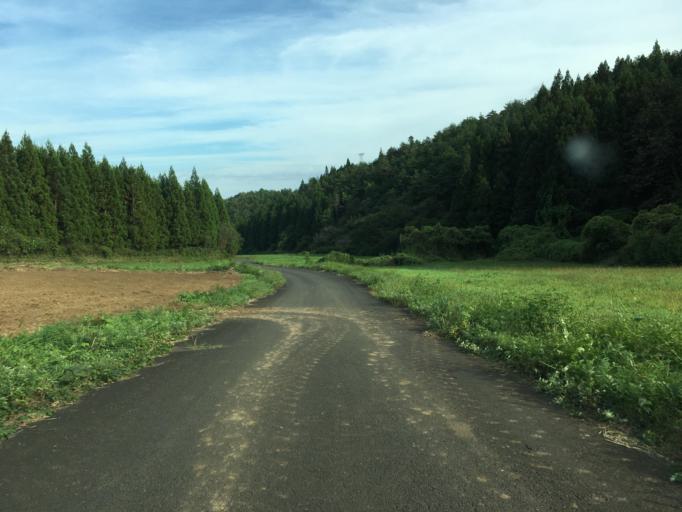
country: JP
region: Fukushima
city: Nihommatsu
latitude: 37.6407
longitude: 140.4052
